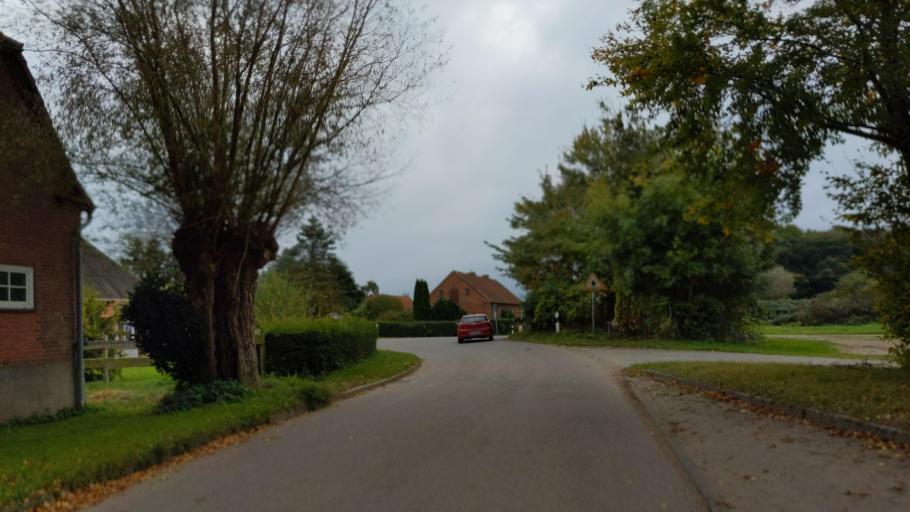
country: DE
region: Schleswig-Holstein
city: Susel
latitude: 54.0721
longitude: 10.7413
